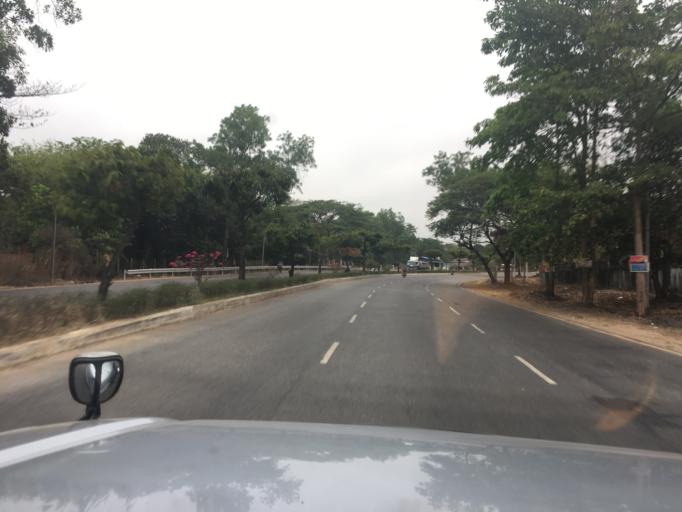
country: MM
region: Bago
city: Thanatpin
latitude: 17.1968
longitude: 96.4005
